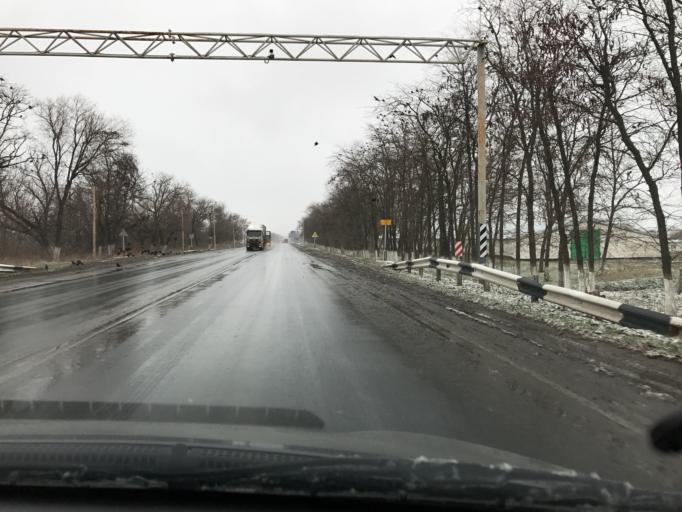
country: RU
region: Rostov
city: Zernograd
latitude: 46.8128
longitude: 40.2914
